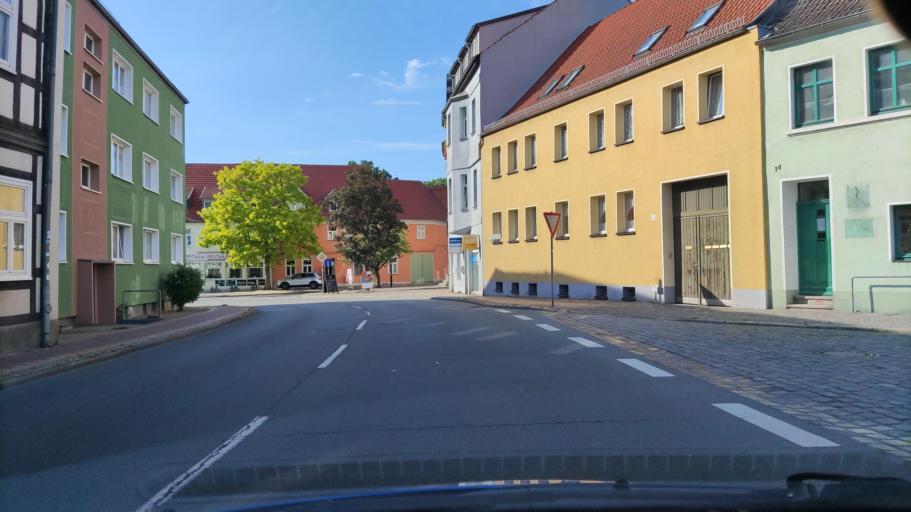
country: DE
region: Saxony-Anhalt
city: Gardelegen
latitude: 52.5272
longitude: 11.3897
